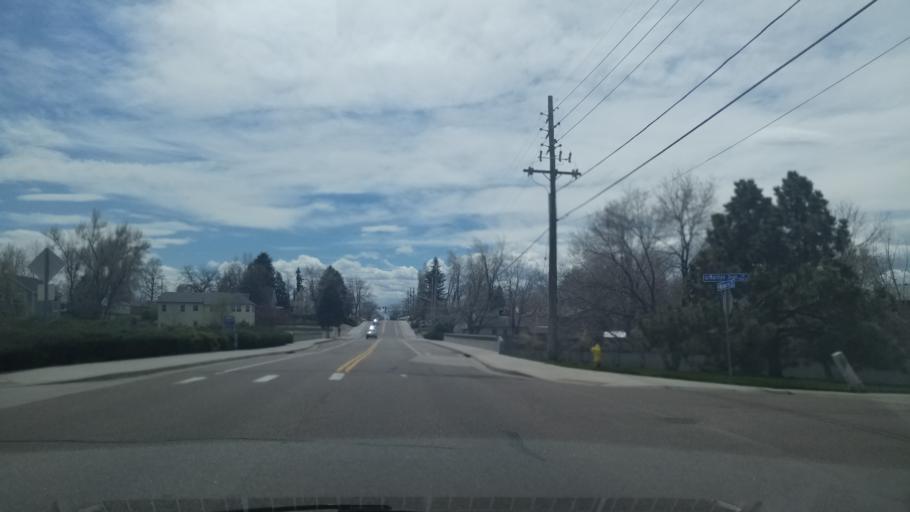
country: US
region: Colorado
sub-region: Jefferson County
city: Arvada
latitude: 39.8050
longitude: -105.0815
